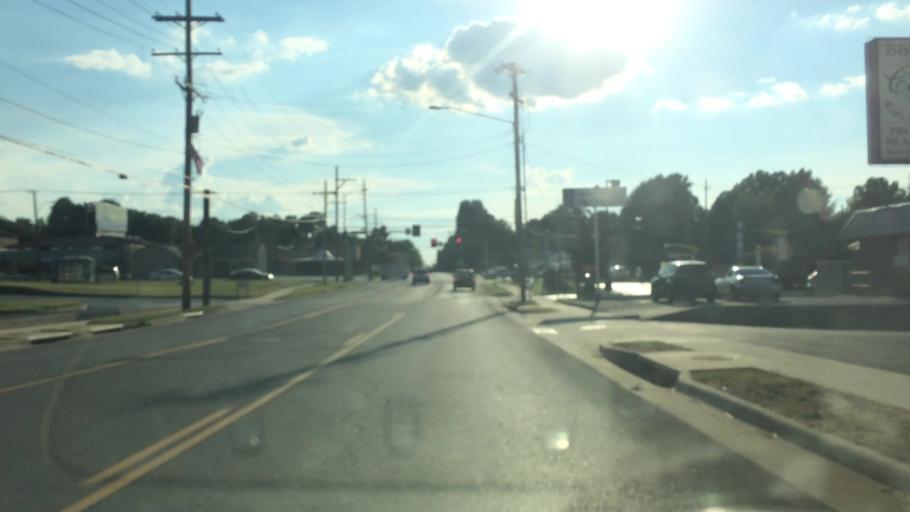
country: US
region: Missouri
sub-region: Greene County
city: Springfield
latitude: 37.2036
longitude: -93.2607
